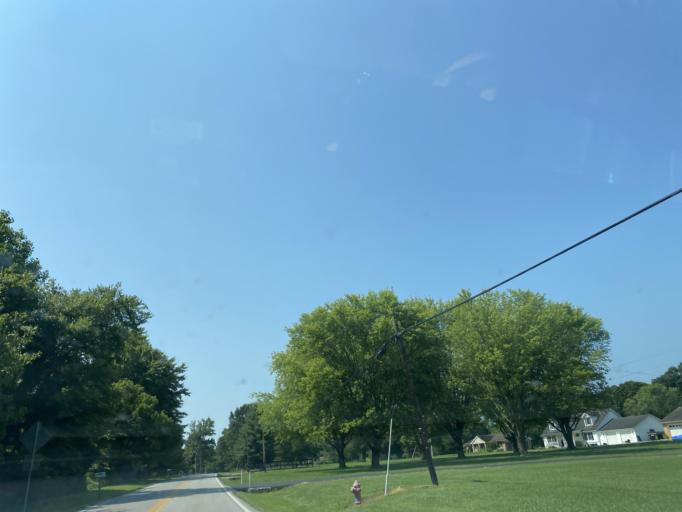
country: US
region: Kentucky
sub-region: Campbell County
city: Claryville
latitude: 38.8841
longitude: -84.4483
